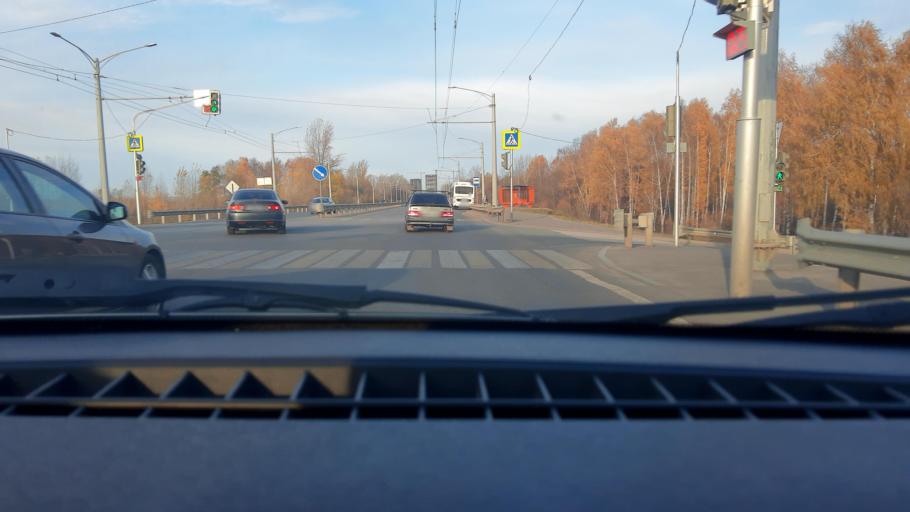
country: RU
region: Bashkortostan
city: Ufa
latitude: 54.7665
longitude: 55.9361
